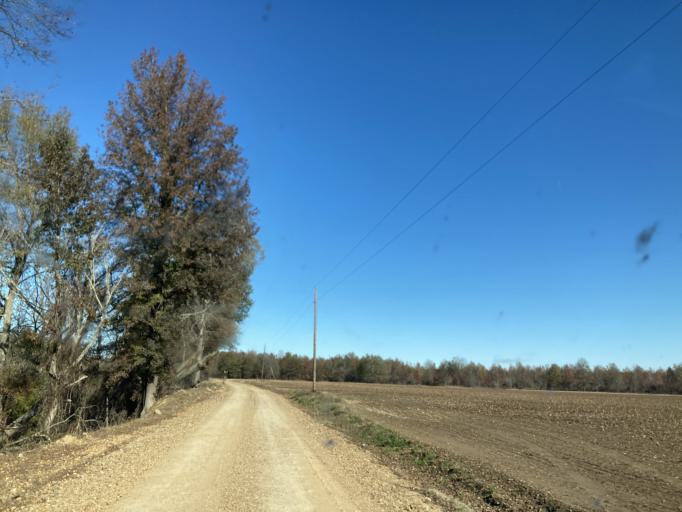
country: US
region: Mississippi
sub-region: Sharkey County
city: Rolling Fork
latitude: 32.7531
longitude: -90.6928
